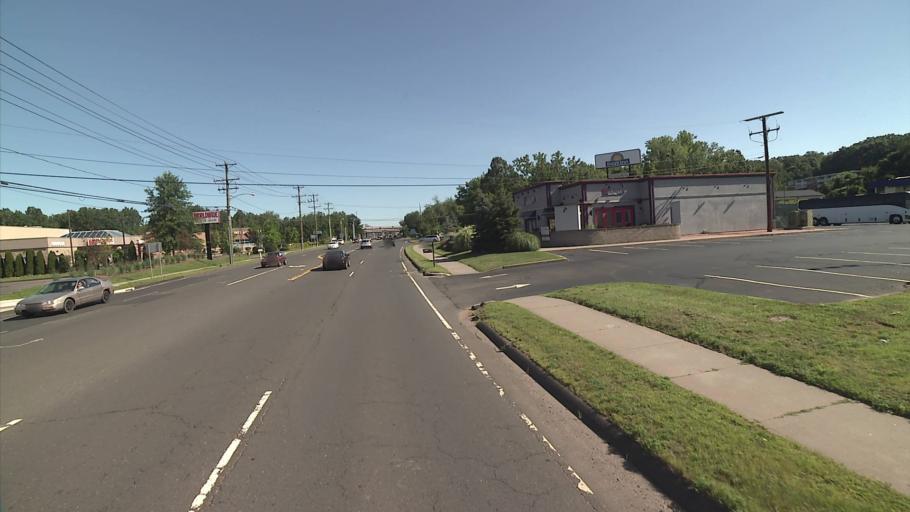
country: US
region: Connecticut
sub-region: Hartford County
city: Plainville
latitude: 41.6290
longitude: -72.8736
